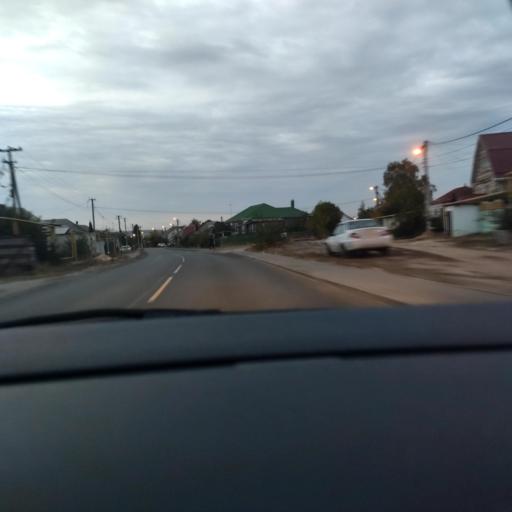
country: RU
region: Voronezj
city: Podgornoye
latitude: 51.7254
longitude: 39.1439
